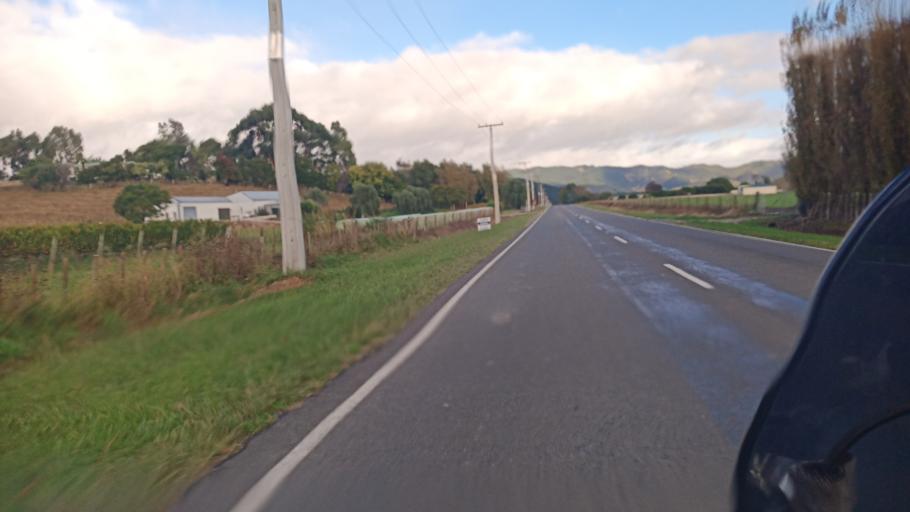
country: NZ
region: Gisborne
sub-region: Gisborne District
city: Gisborne
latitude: -38.6330
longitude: 177.8713
